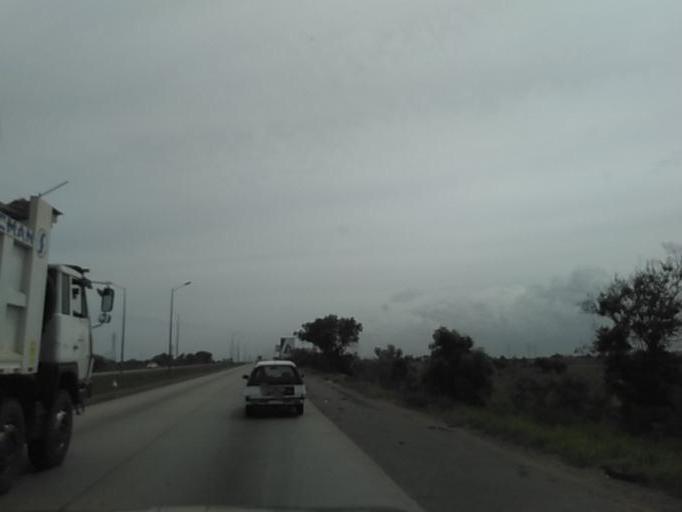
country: GH
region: Greater Accra
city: Tema
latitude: 5.6707
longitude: -0.0511
